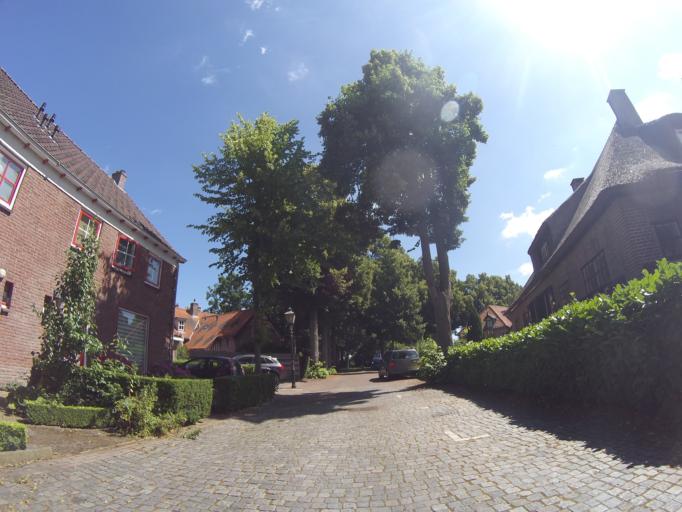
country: NL
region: Utrecht
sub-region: Stichtse Vecht
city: Spechtenkamp
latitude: 52.1206
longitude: 4.9970
